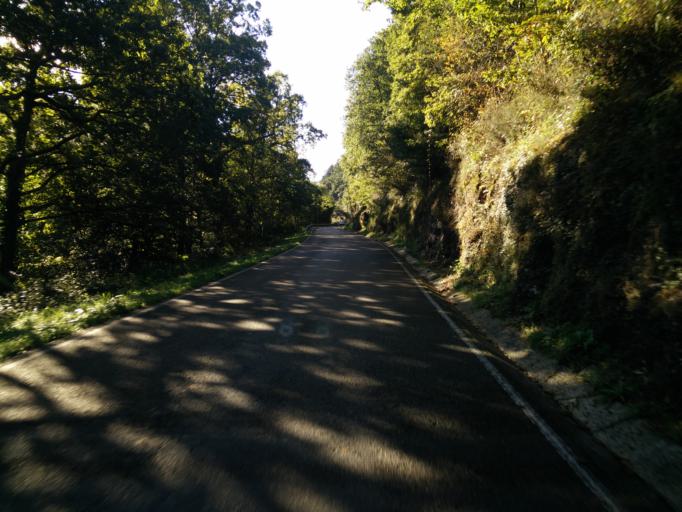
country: ES
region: Cantabria
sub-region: Provincia de Cantabria
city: San Pedro del Romeral
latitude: 43.1405
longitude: -3.8168
